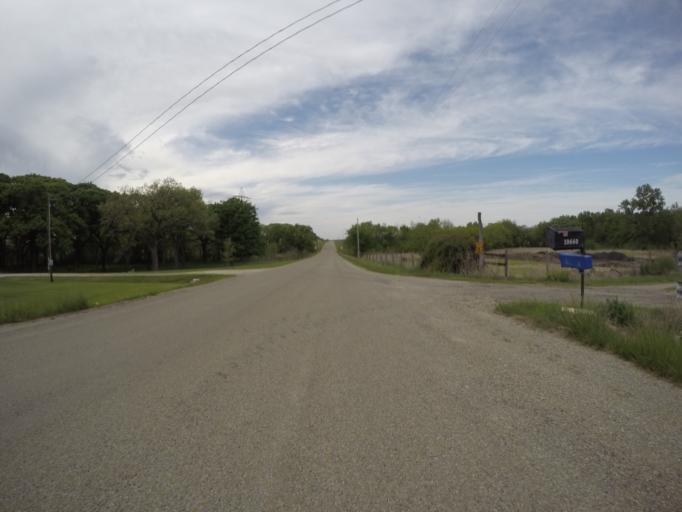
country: US
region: Kansas
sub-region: Riley County
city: Ogden
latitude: 39.0102
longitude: -96.6038
